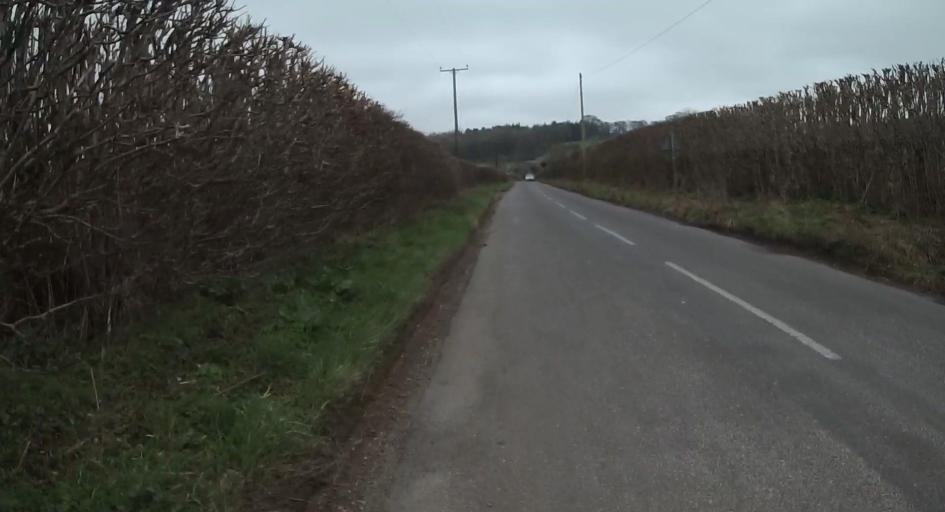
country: GB
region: England
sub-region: Hampshire
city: Basingstoke
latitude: 51.1902
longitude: -1.1144
